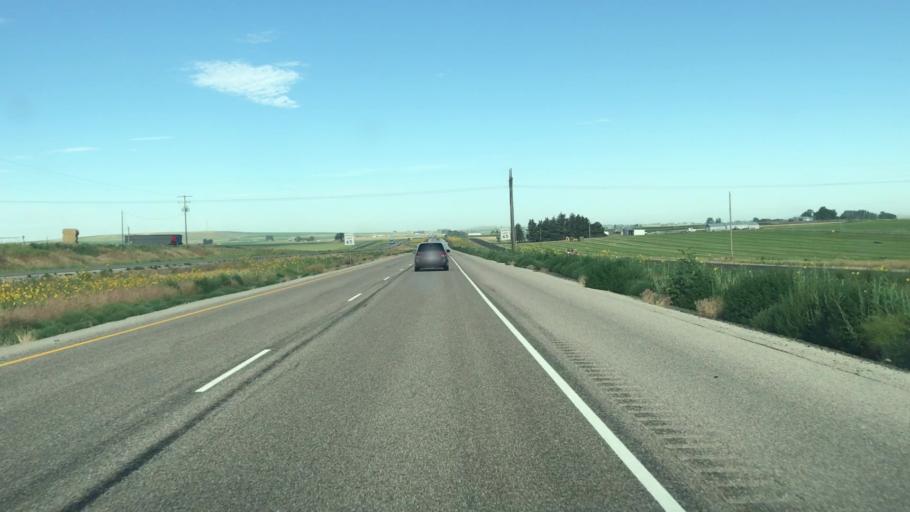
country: US
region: Idaho
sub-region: Cassia County
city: Burley
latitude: 42.5764
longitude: -114.0129
